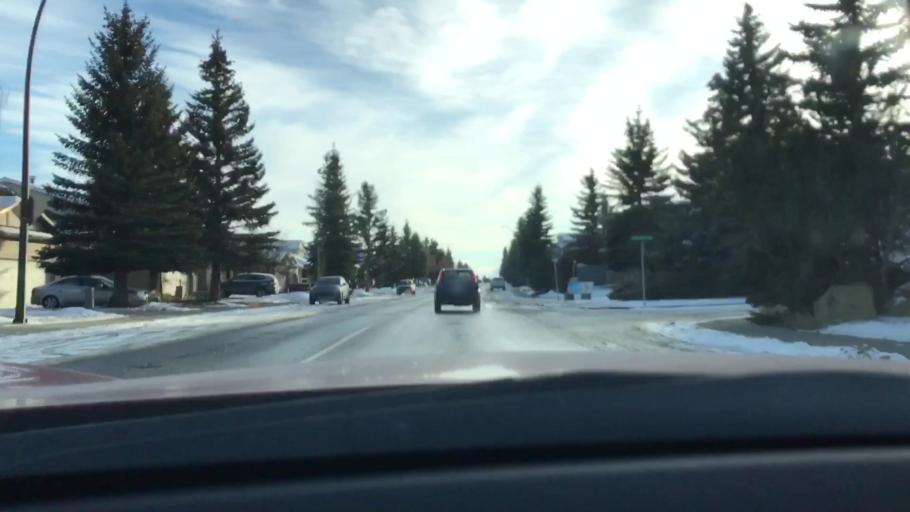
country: CA
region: Alberta
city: Calgary
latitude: 51.0303
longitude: -114.1703
